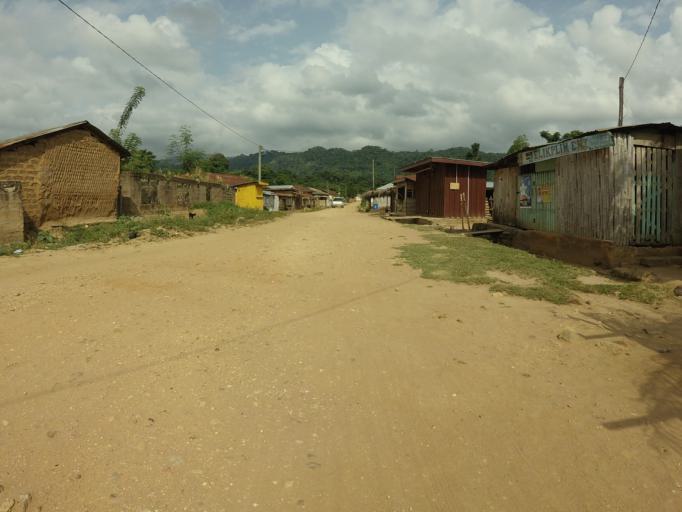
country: GH
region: Volta
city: Kpandu
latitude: 6.8947
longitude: 0.4317
